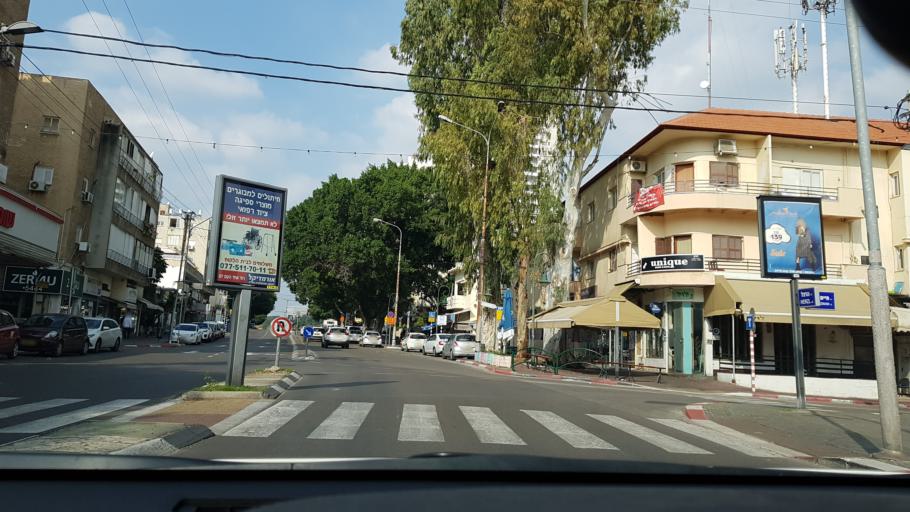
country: IL
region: Central District
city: Ness Ziona
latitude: 31.8987
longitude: 34.8103
